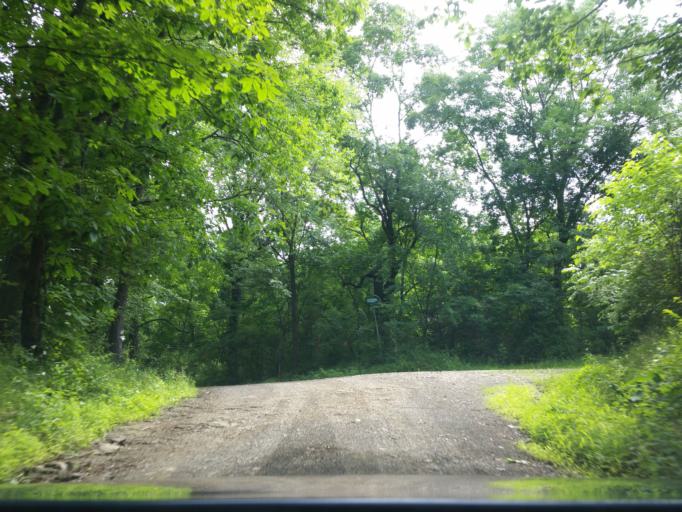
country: US
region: Pennsylvania
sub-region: Lebanon County
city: Jonestown
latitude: 40.4314
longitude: -76.5329
